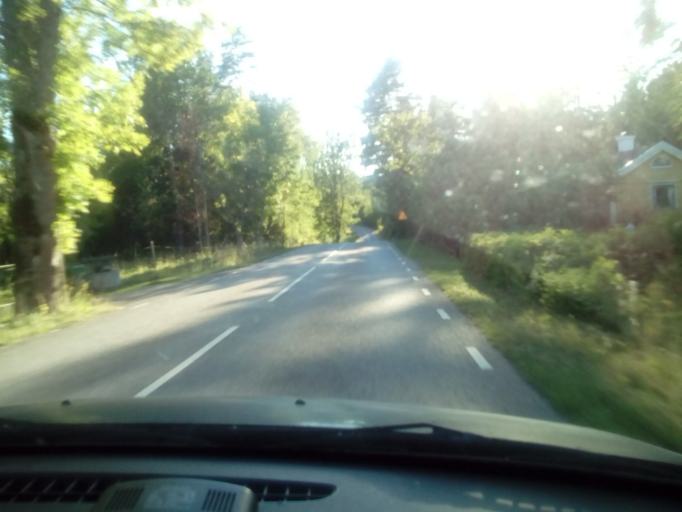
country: SE
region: Kalmar
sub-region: Vasterviks Kommun
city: Gamleby
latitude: 57.8047
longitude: 16.4217
